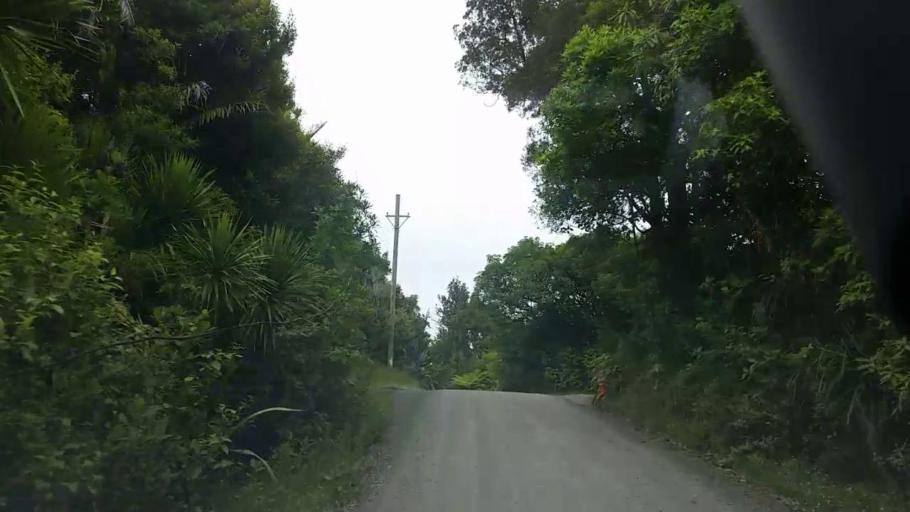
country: NZ
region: Auckland
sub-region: Auckland
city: Titirangi
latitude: -37.0269
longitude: 174.5294
